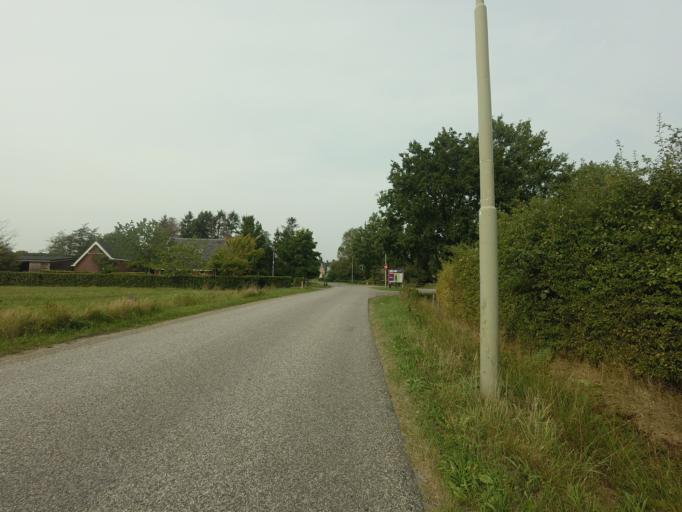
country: NL
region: Drenthe
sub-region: Gemeente Tynaarlo
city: Vries
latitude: 53.1259
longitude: 6.5677
